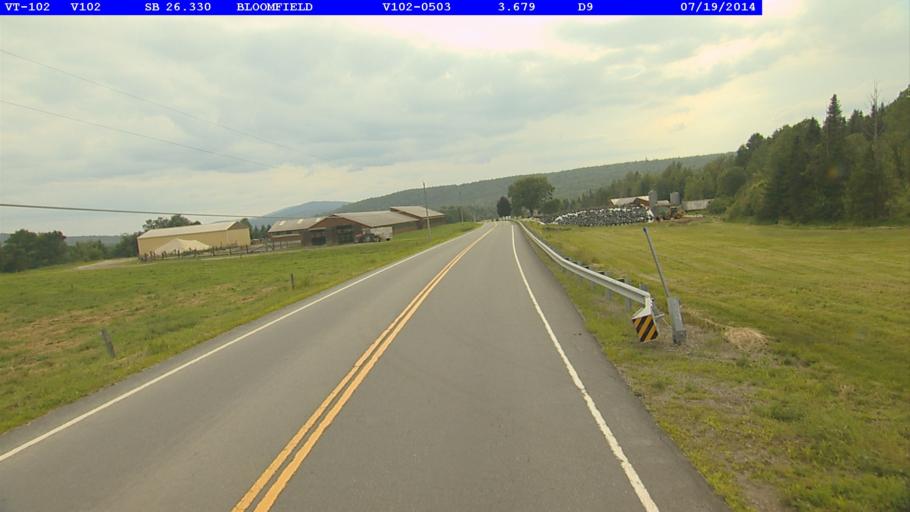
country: US
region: New Hampshire
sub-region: Coos County
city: Stratford
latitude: 44.7862
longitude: -71.5849
